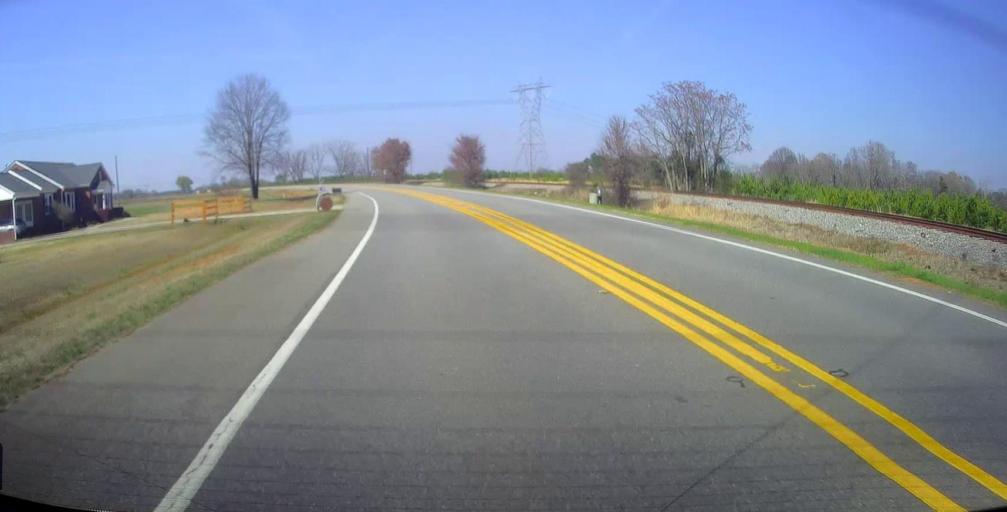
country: US
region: Georgia
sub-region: Jones County
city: Gray
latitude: 33.0295
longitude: -83.5364
